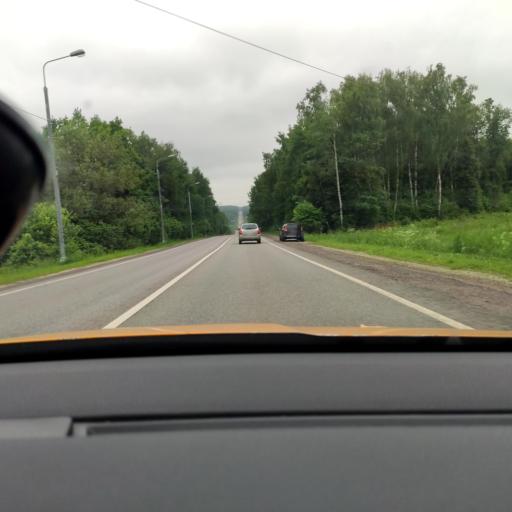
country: RU
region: Moskovskaya
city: Danki
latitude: 54.9237
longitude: 37.5072
